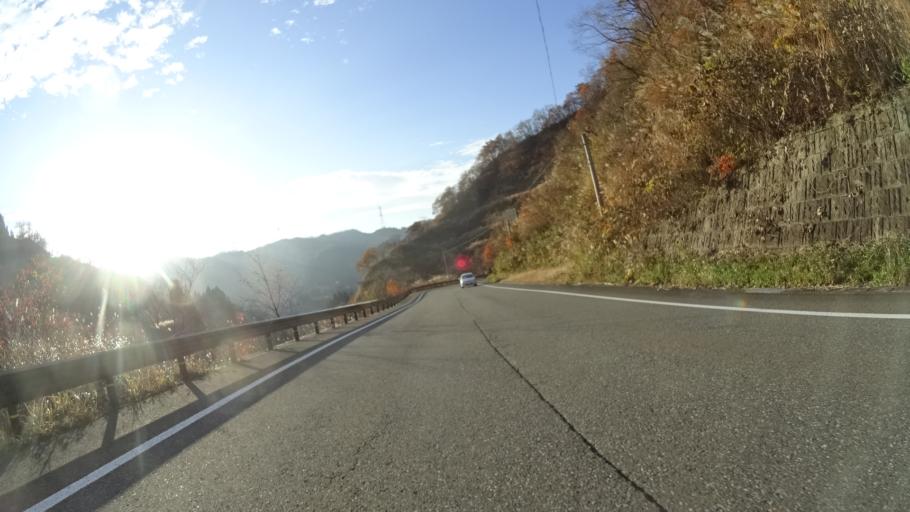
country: JP
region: Niigata
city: Shiozawa
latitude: 36.9845
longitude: 138.7565
